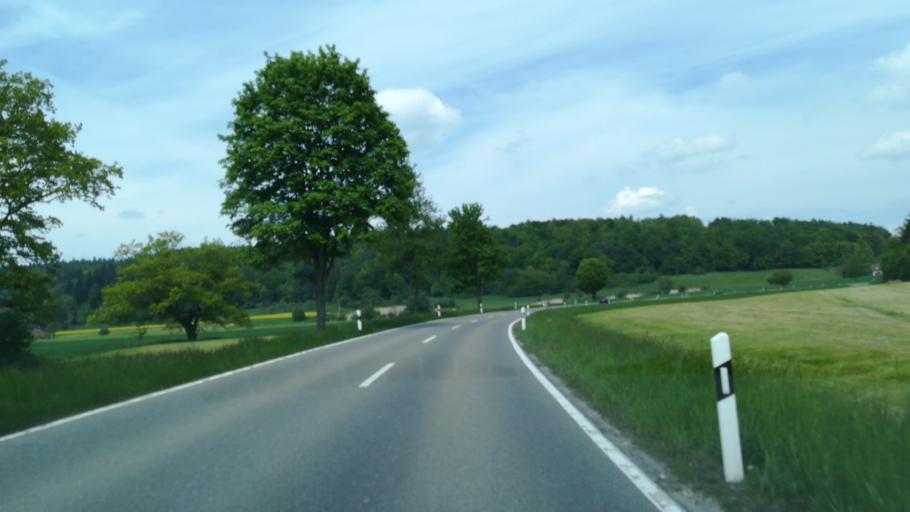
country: DE
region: Baden-Wuerttemberg
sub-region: Freiburg Region
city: Stockach
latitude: 47.8699
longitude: 9.0254
